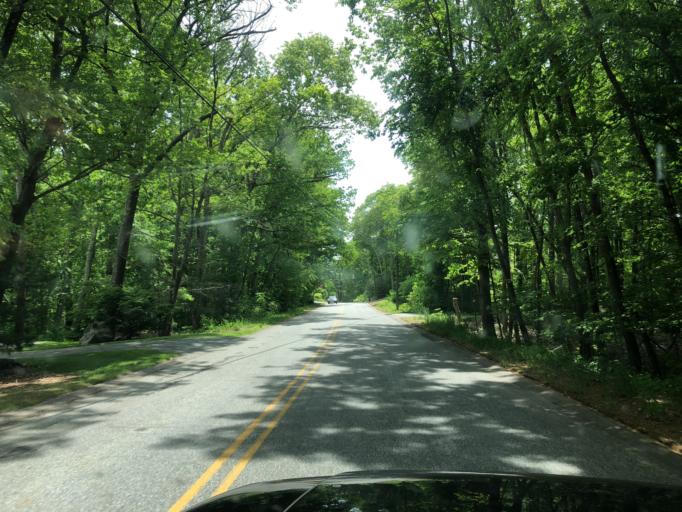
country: US
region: Connecticut
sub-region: Windham County
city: North Grosvenor Dale
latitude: 41.9787
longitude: -71.8894
